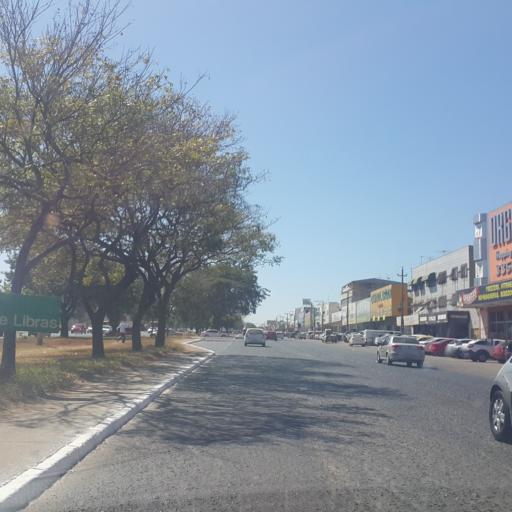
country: BR
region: Federal District
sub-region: Brasilia
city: Brasilia
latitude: -15.8052
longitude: -48.0744
